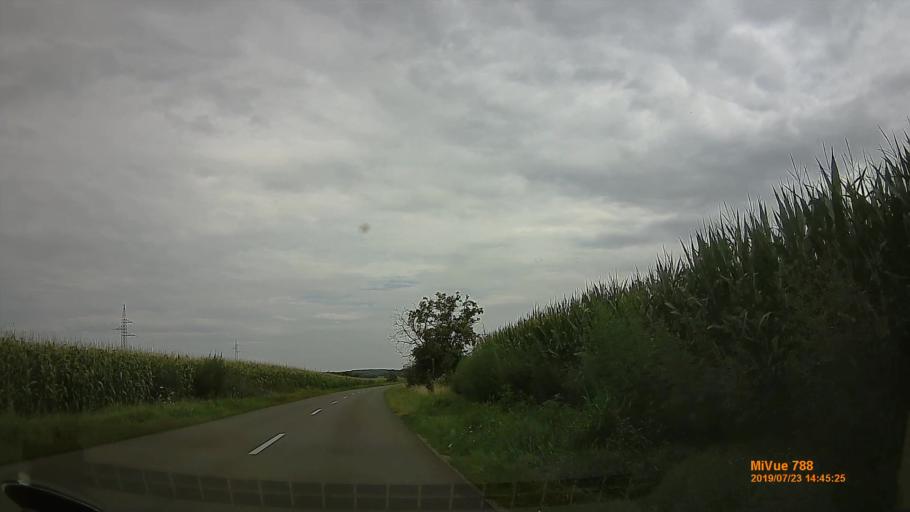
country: HU
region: Szabolcs-Szatmar-Bereg
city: Nyiregyhaza
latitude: 47.9290
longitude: 21.6761
